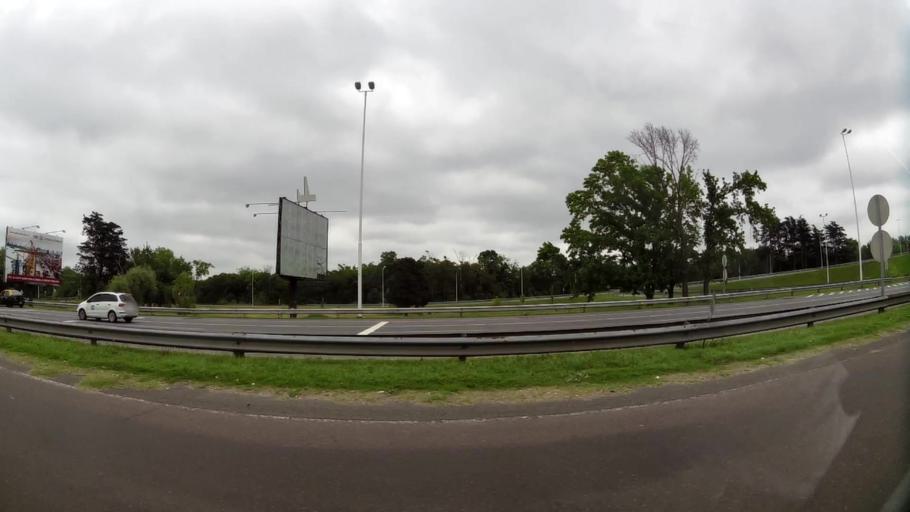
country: AR
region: Buenos Aires
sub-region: Partido de Ezeiza
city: Ezeiza
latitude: -34.8073
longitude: -58.5433
